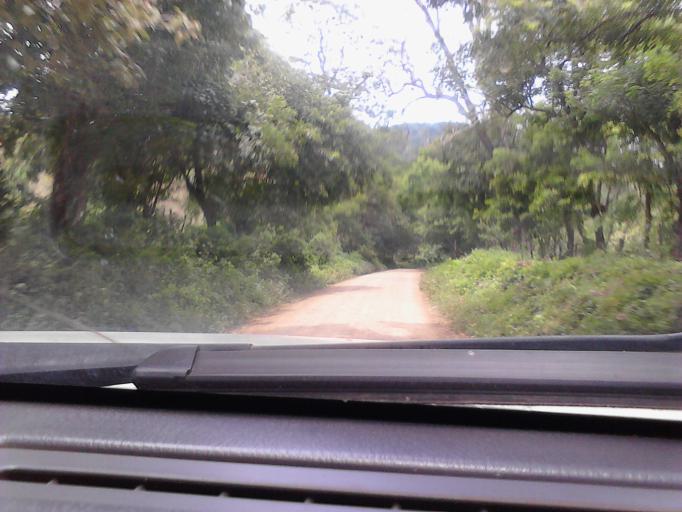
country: NI
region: Matagalpa
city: Terrabona
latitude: 12.7060
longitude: -85.9506
